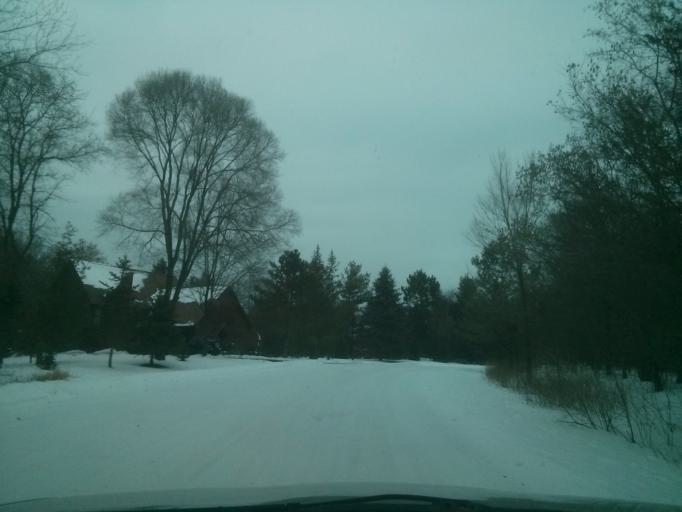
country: US
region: Minnesota
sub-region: Washington County
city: Lakeland
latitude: 44.9397
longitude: -92.7752
